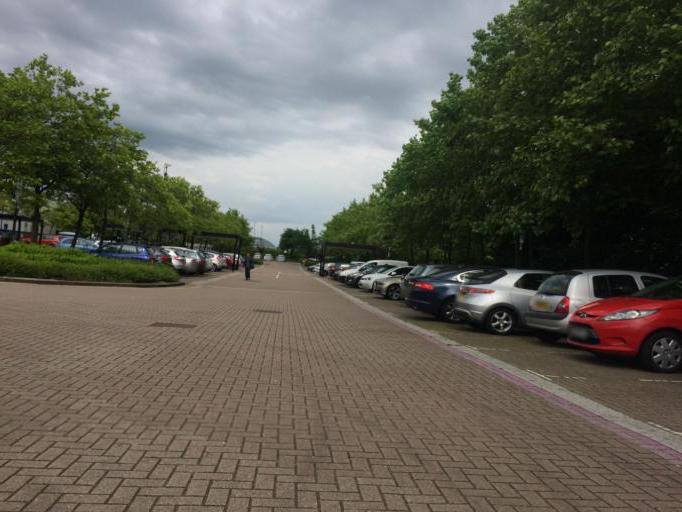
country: GB
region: England
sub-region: Milton Keynes
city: Milton Keynes
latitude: 52.0320
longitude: -0.7685
